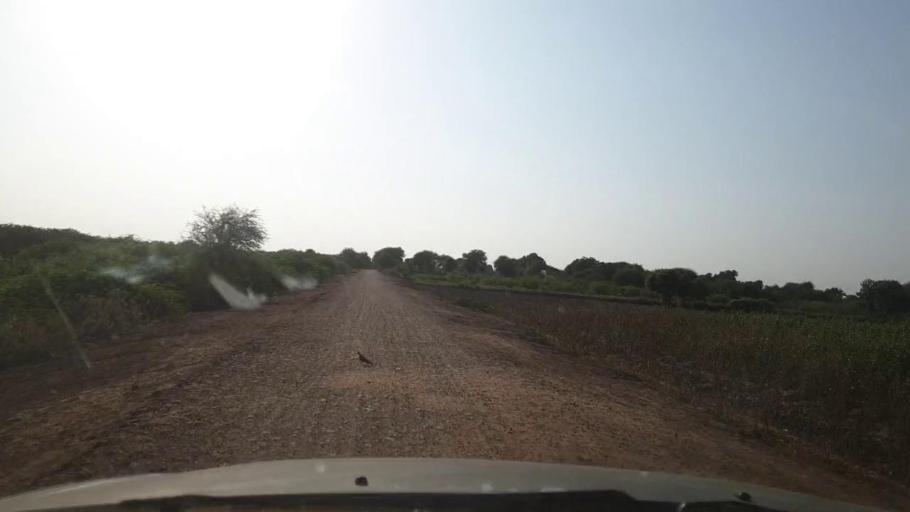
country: PK
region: Sindh
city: Tando Ghulam Ali
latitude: 25.1166
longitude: 68.9367
